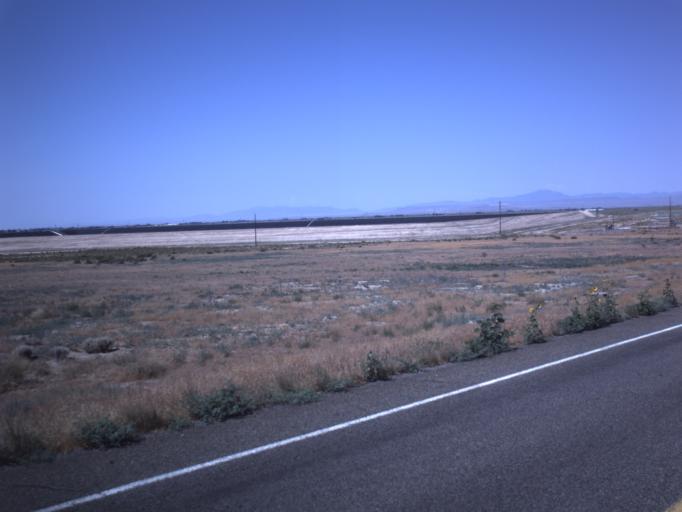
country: US
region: Utah
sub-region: Millard County
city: Delta
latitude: 39.4904
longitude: -112.5575
